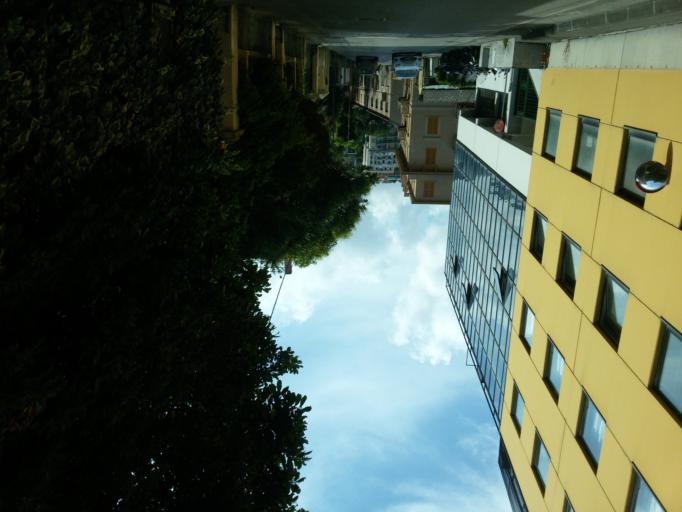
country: IT
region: Liguria
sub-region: Provincia di Genova
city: Genoa
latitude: 44.3975
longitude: 8.9863
